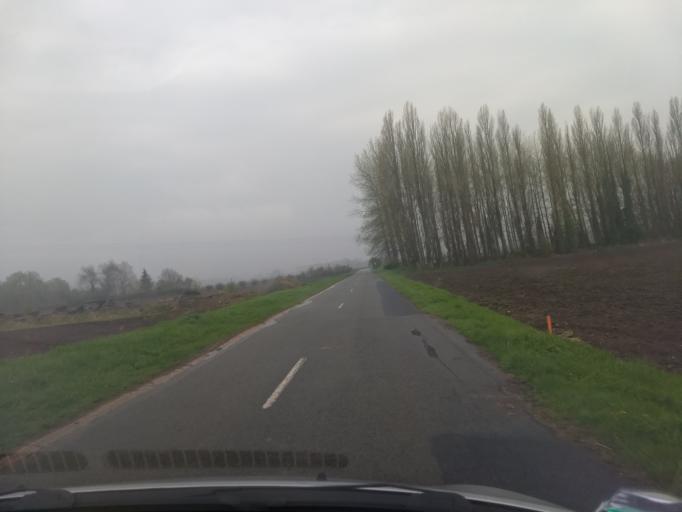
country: FR
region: Nord-Pas-de-Calais
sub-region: Departement du Pas-de-Calais
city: Vitry-en-Artois
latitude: 50.3224
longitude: 2.9726
